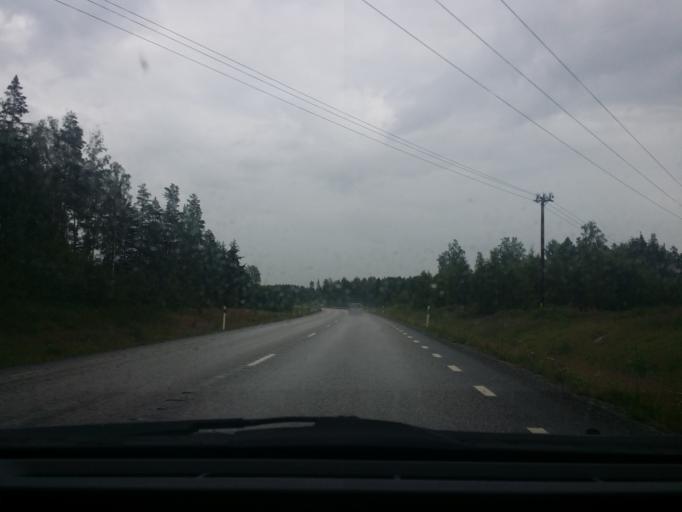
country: SE
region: OErebro
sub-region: Lindesbergs Kommun
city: Frovi
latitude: 59.4600
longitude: 15.4376
